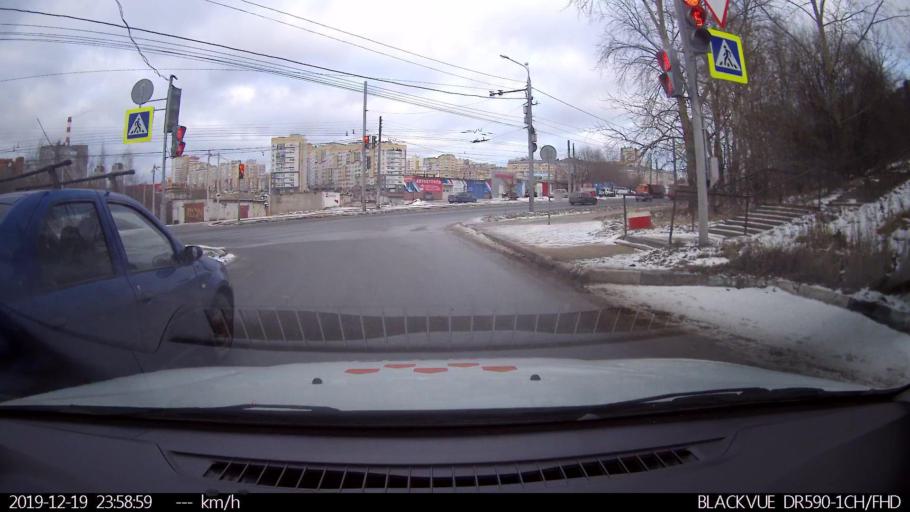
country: RU
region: Jaroslavl
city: Kukoboy
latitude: 58.8643
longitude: 39.6407
